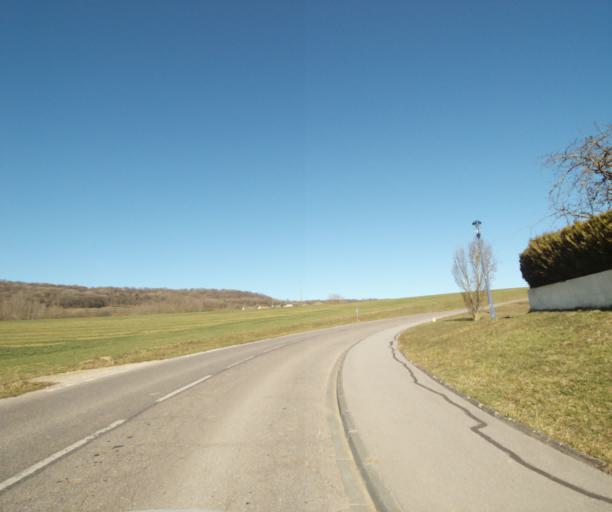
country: FR
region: Lorraine
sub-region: Departement de Meurthe-et-Moselle
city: Ludres
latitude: 48.6143
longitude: 6.1590
